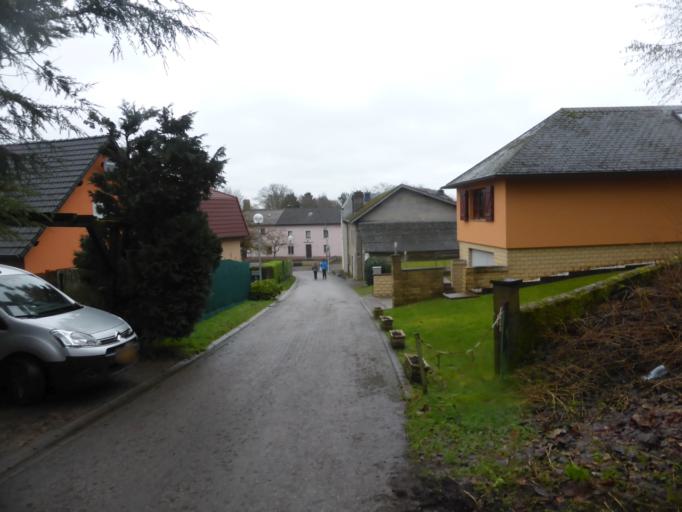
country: LU
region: Luxembourg
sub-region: Canton de Mersch
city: Lorentzweiler
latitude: 49.7018
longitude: 6.1644
